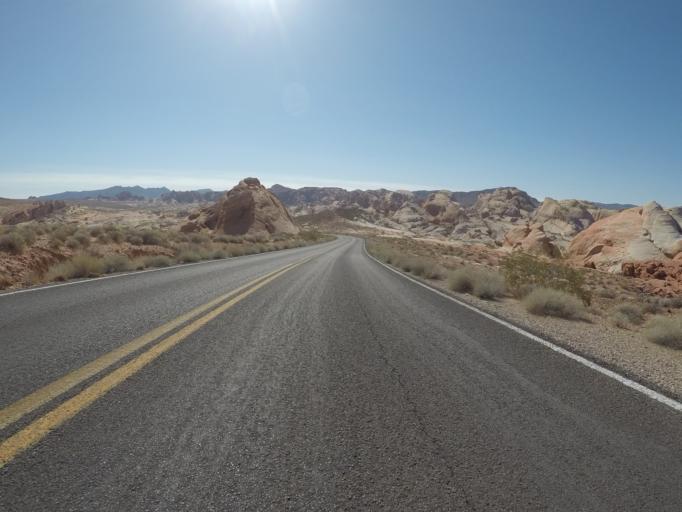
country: US
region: Nevada
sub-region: Clark County
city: Moapa Valley
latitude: 36.4851
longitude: -114.5270
